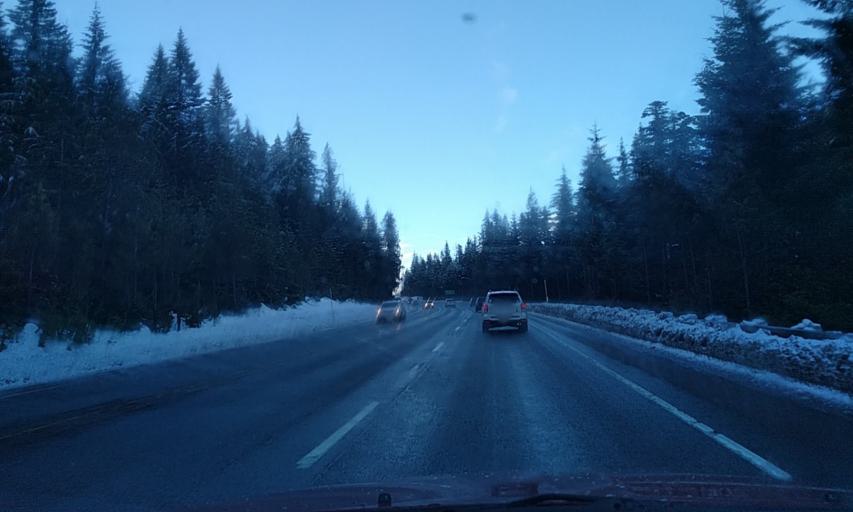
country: US
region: Oregon
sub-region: Clackamas County
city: Mount Hood Village
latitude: 45.3037
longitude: -121.7830
